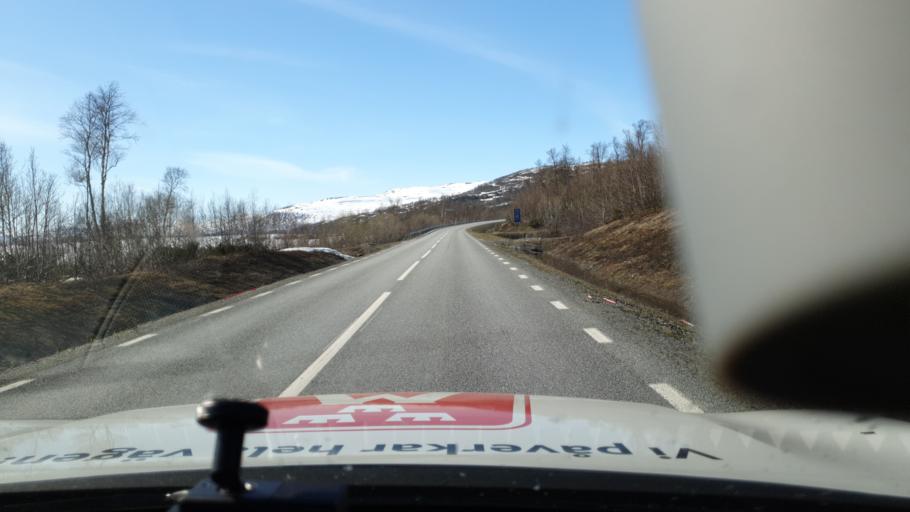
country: NO
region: Nordland
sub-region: Rana
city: Mo i Rana
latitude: 66.0916
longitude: 14.8554
